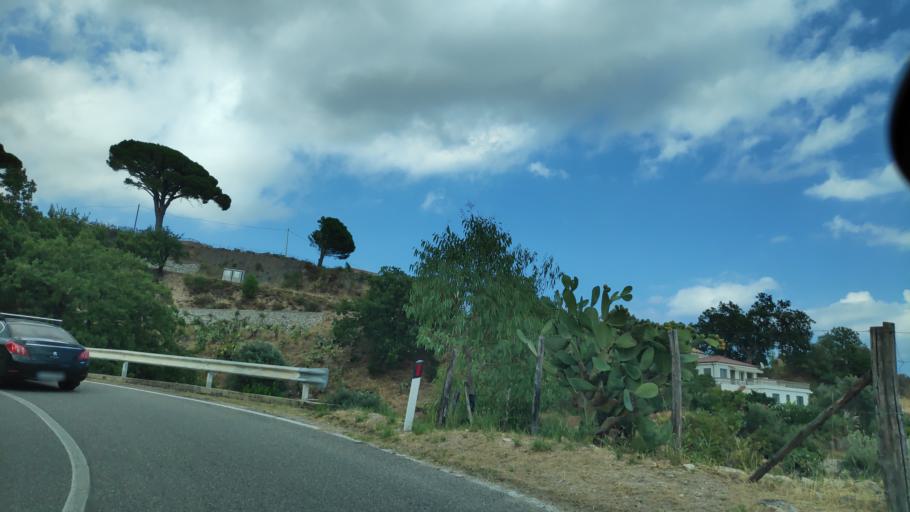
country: IT
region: Calabria
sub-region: Provincia di Catanzaro
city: Santa Caterina dello Ionio
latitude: 38.5301
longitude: 16.5246
